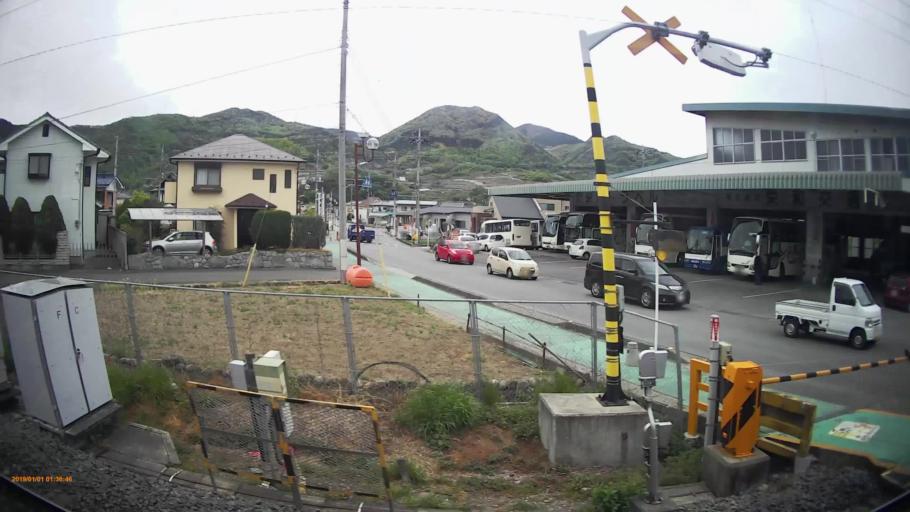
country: JP
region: Yamanashi
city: Isawa
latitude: 35.6725
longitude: 138.6576
